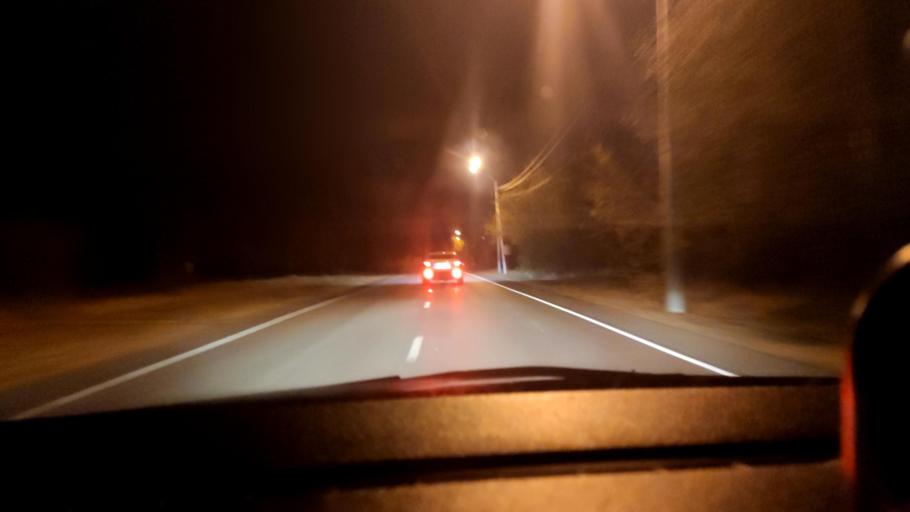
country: RU
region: Voronezj
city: Pridonskoy
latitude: 51.6127
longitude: 39.0519
